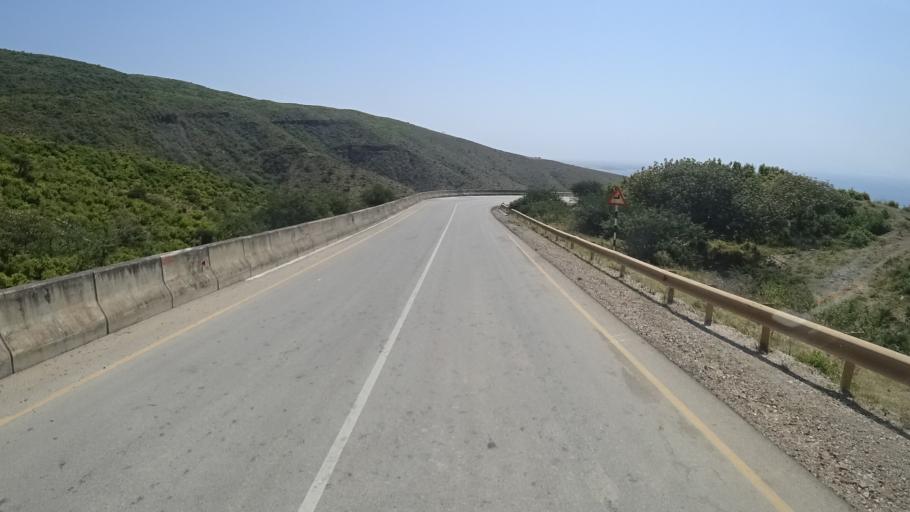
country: OM
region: Zufar
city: Salalah
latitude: 17.0501
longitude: 54.6116
